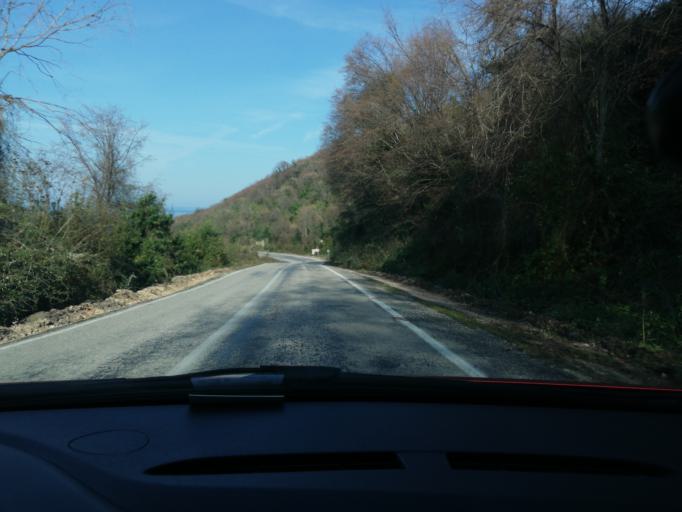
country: TR
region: Bartin
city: Kurucasile
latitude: 41.8539
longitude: 32.7760
